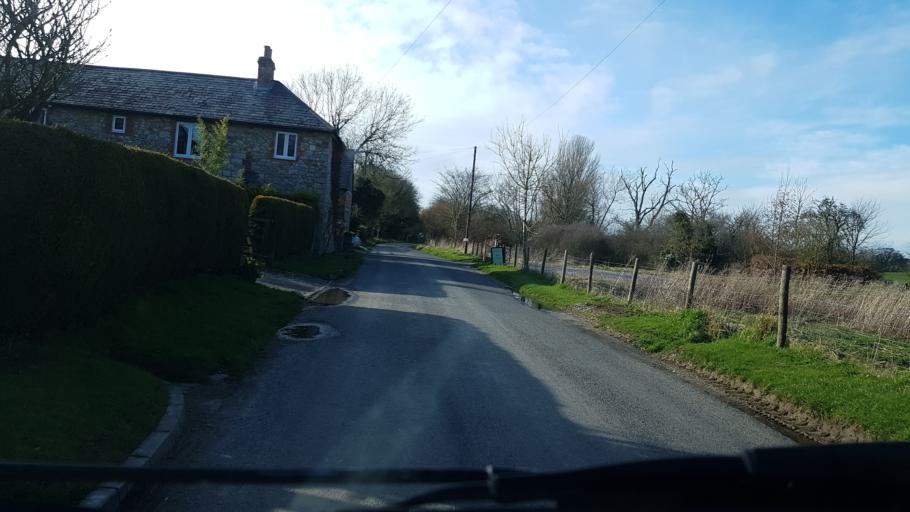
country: GB
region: England
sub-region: Wiltshire
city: Avebury
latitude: 51.4072
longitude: -1.8323
